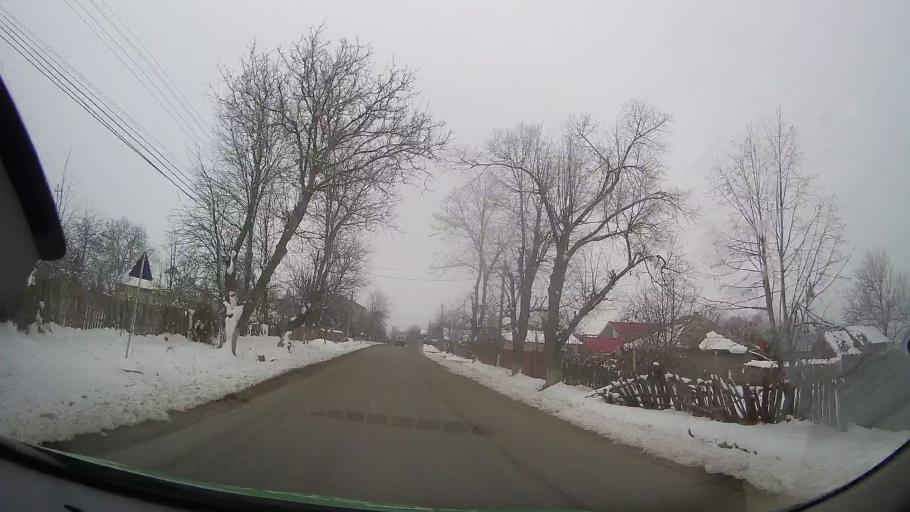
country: RO
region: Bacau
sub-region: Comuna Vultureni
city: Vultureni
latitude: 46.4047
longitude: 27.2728
